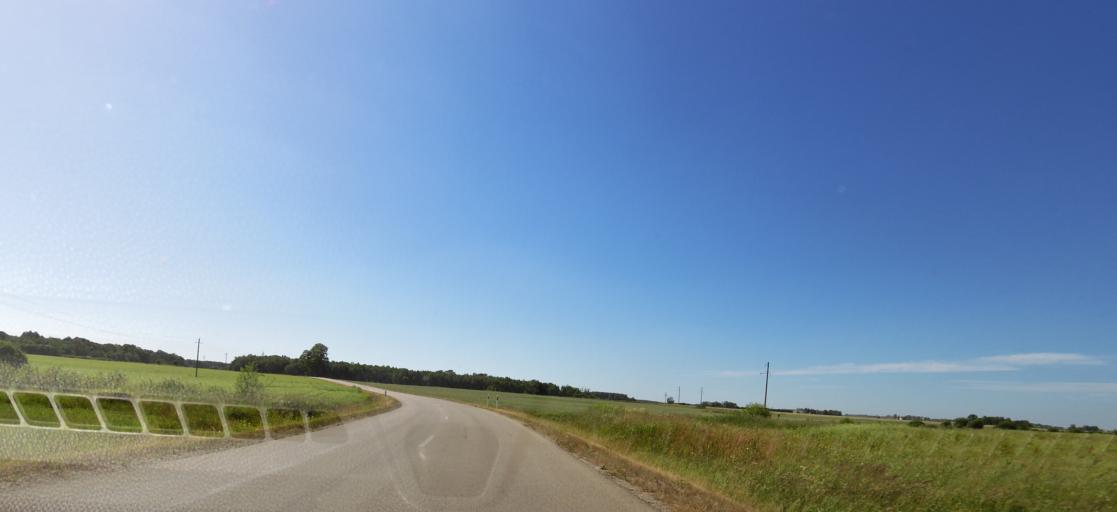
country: LT
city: Vabalninkas
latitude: 56.0026
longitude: 24.6611
